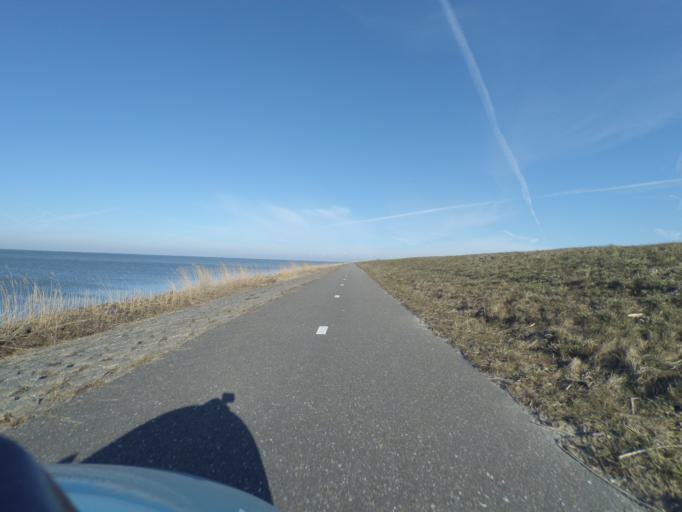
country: NL
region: North Holland
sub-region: Gemeente Naarden
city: Naarden
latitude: 52.3485
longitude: 5.1343
